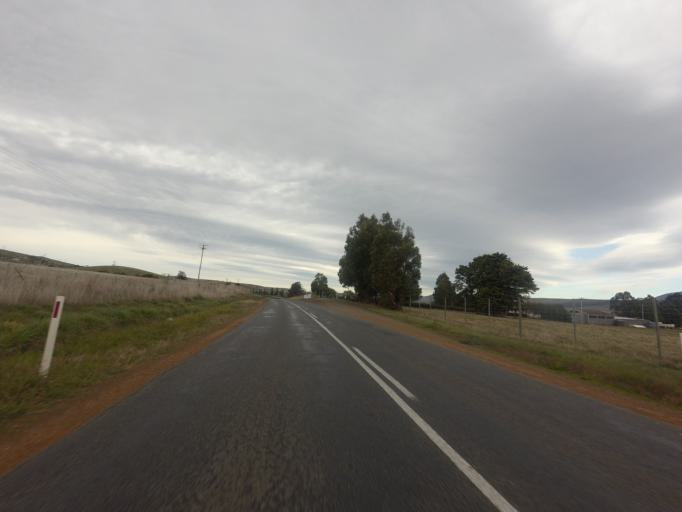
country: AU
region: Tasmania
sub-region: Derwent Valley
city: New Norfolk
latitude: -42.5133
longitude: 146.7433
